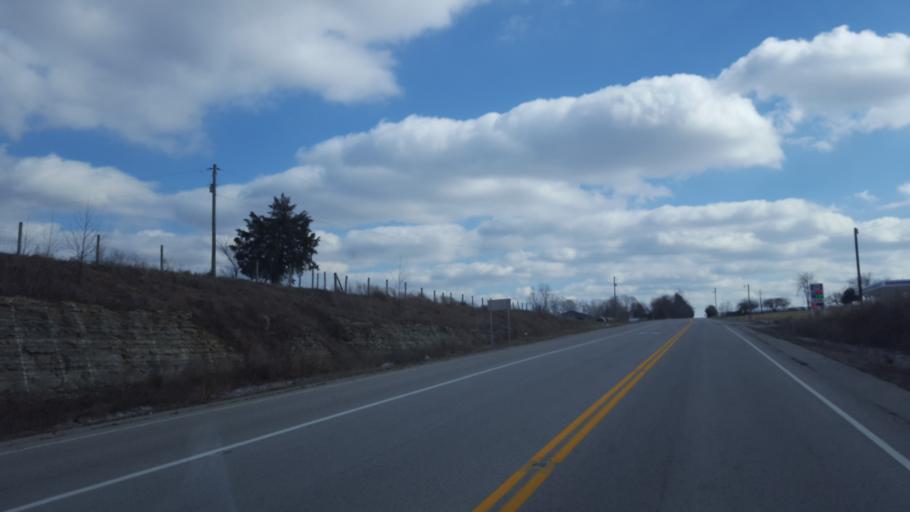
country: US
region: Kentucky
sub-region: Owen County
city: Owenton
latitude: 38.4728
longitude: -84.9491
